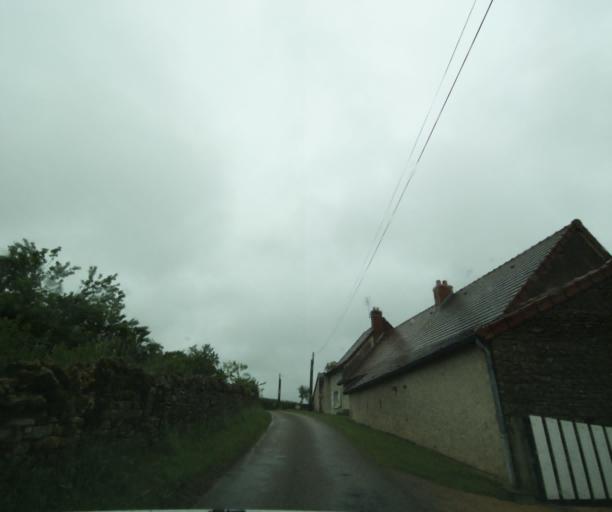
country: FR
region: Bourgogne
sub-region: Departement de Saone-et-Loire
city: Charolles
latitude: 46.3985
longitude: 4.2702
